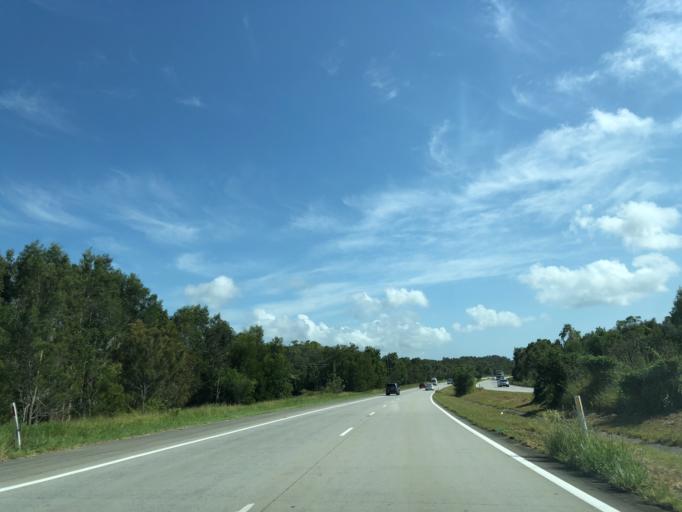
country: AU
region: New South Wales
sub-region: Byron Shire
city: Brunswick Heads
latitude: -28.5707
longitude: 153.5407
